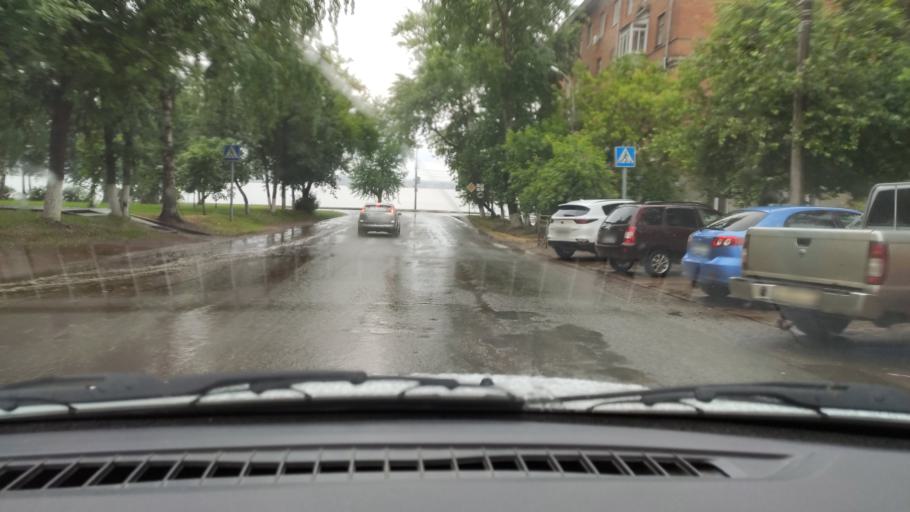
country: RU
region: Udmurtiya
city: Votkinsk
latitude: 57.0618
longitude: 53.9885
